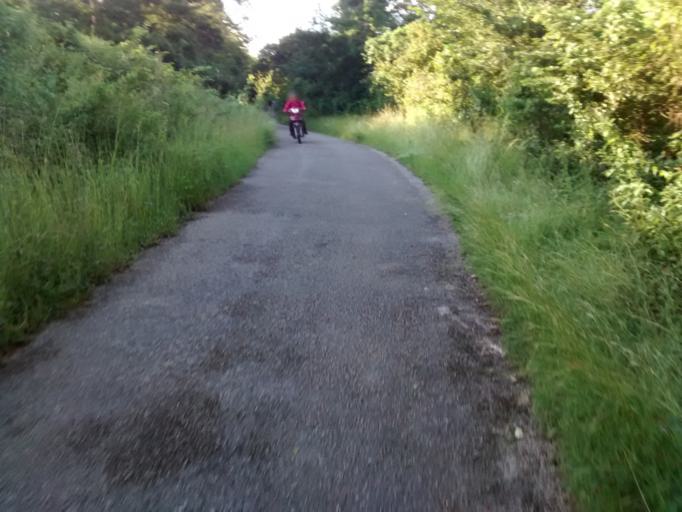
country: MX
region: Yucatan
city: Valladolid
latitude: 20.7157
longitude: -88.2215
